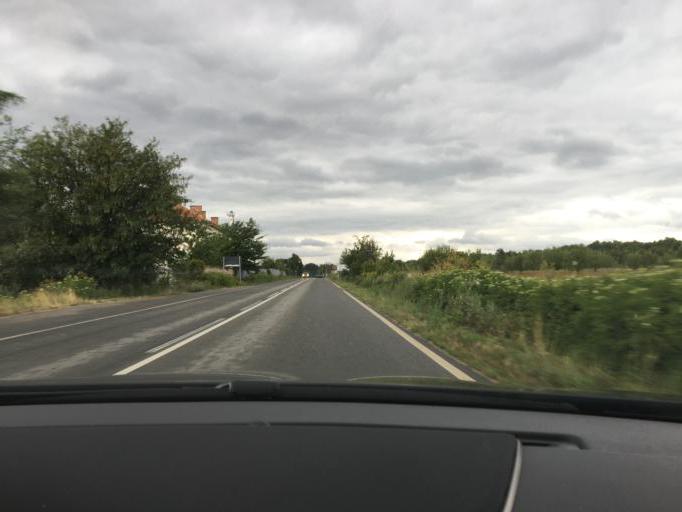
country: BG
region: Kyustendil
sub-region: Obshtina Kyustendil
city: Kyustendil
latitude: 42.2577
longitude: 22.8615
